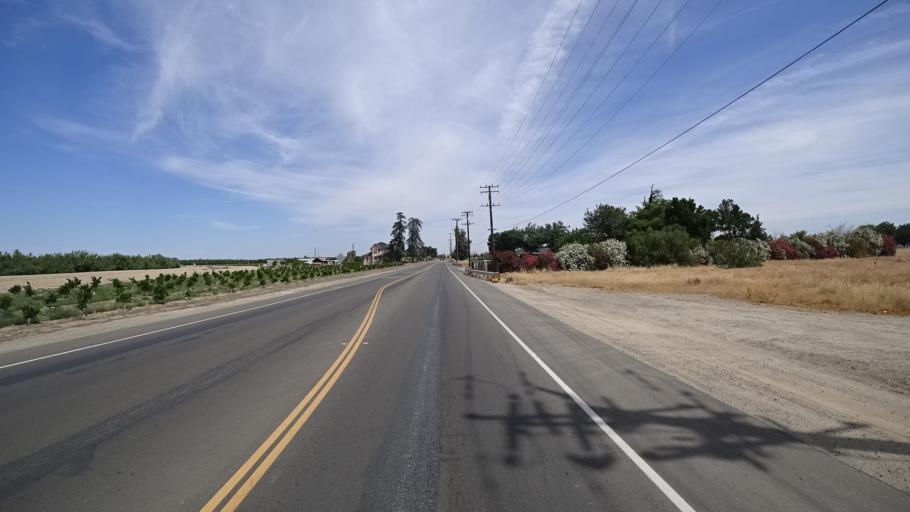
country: US
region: California
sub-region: Kings County
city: Armona
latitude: 36.3287
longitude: -119.6911
